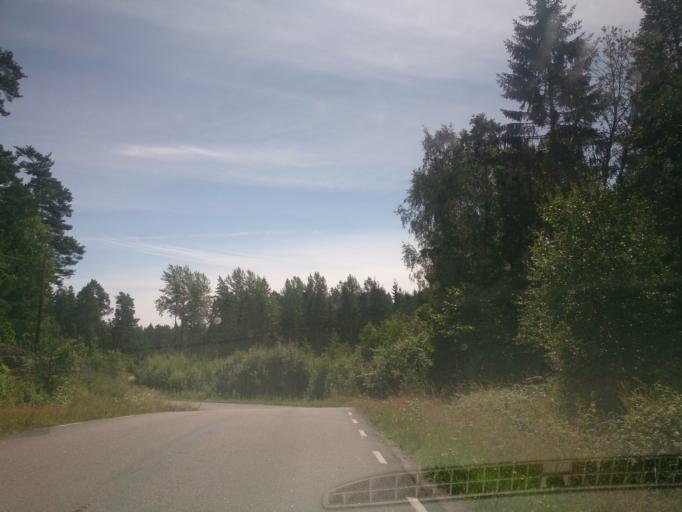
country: SE
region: OEstergoetland
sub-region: Valdemarsviks Kommun
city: Valdemarsvik
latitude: 58.3247
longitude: 16.6424
